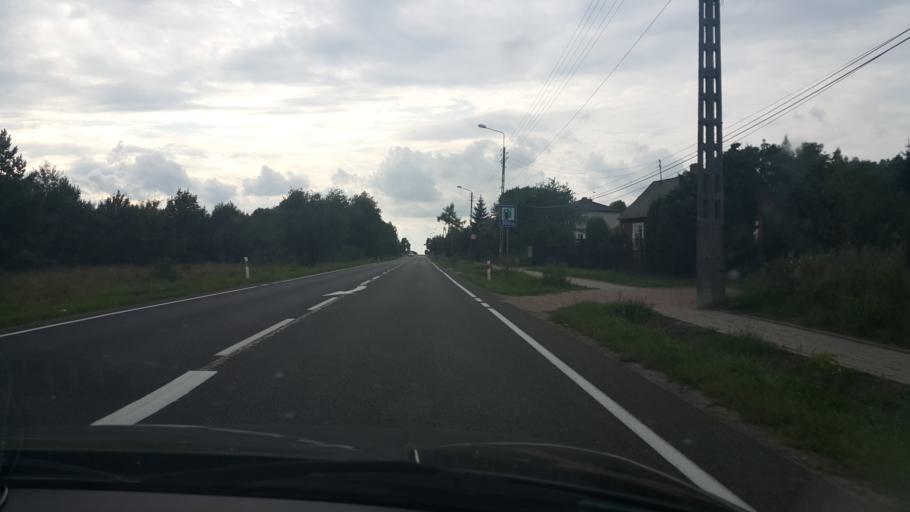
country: PL
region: Swietokrzyskie
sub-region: Powiat skarzyski
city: Blizyn
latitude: 51.1012
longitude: 20.7877
